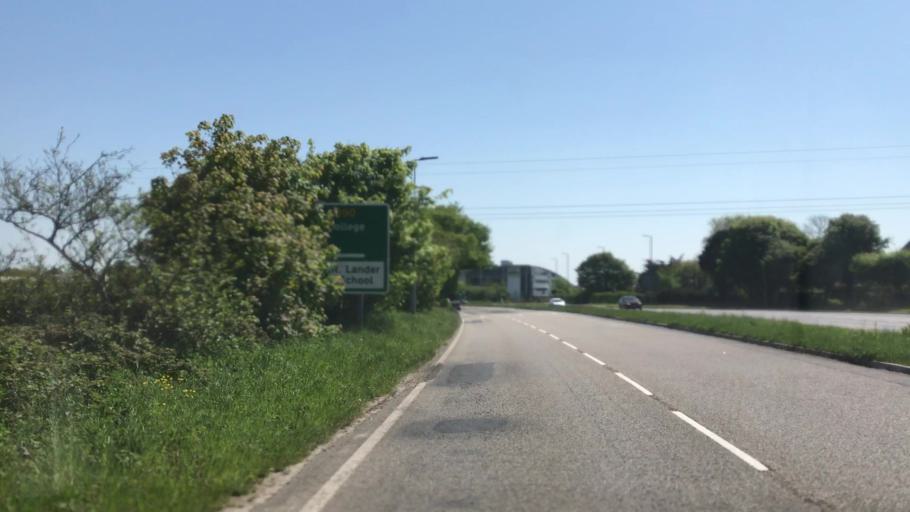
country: GB
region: England
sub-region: Cornwall
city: Truro
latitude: 50.2638
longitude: -5.1083
